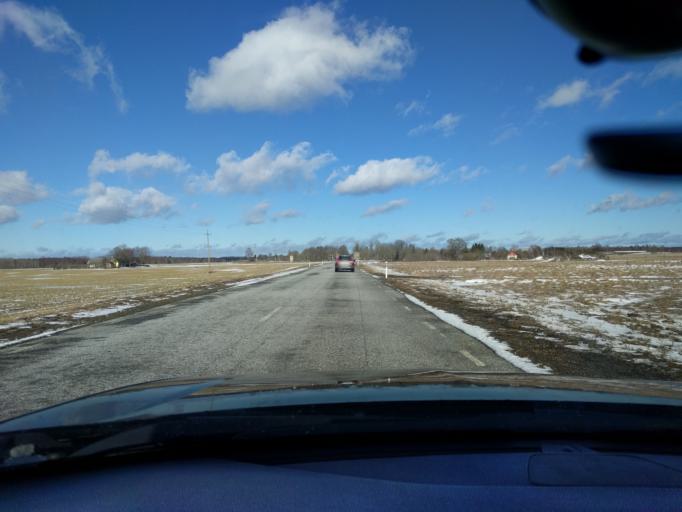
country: EE
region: Harju
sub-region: Raasiku vald
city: Raasiku
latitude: 59.3918
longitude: 25.1875
